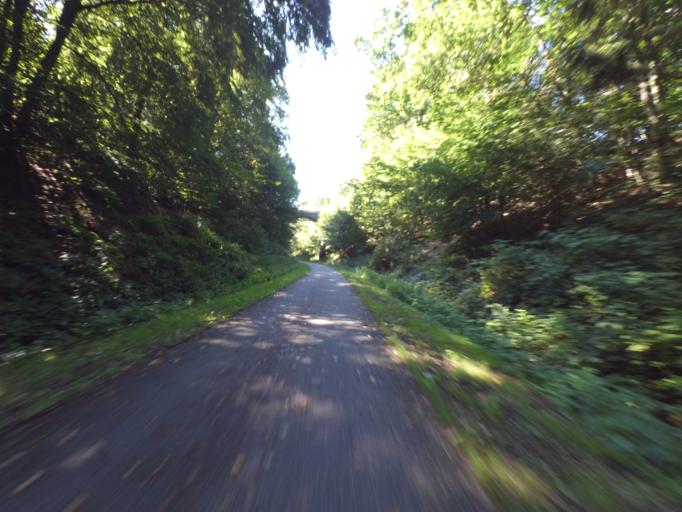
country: DE
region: Rheinland-Pfalz
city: Pantenburg
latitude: 50.1006
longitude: 6.8403
